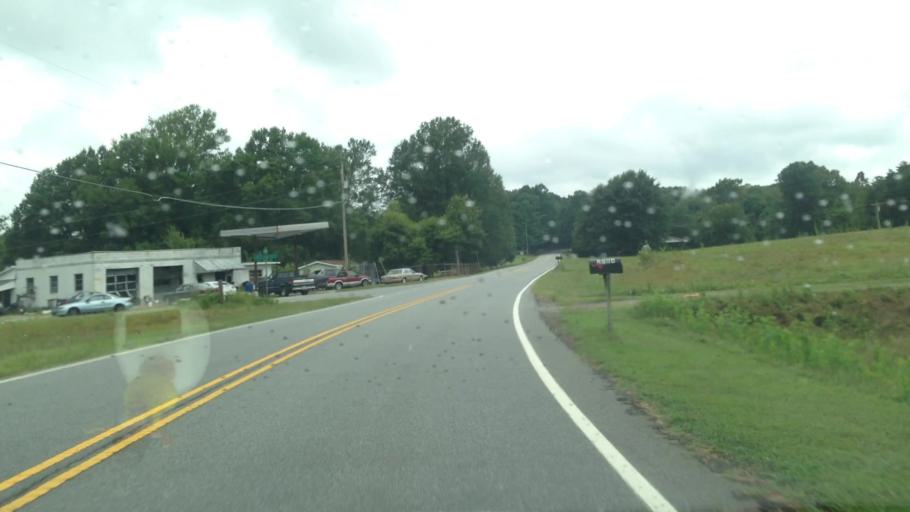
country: US
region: North Carolina
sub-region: Rockingham County
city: Mayodan
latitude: 36.4059
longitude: -80.0489
